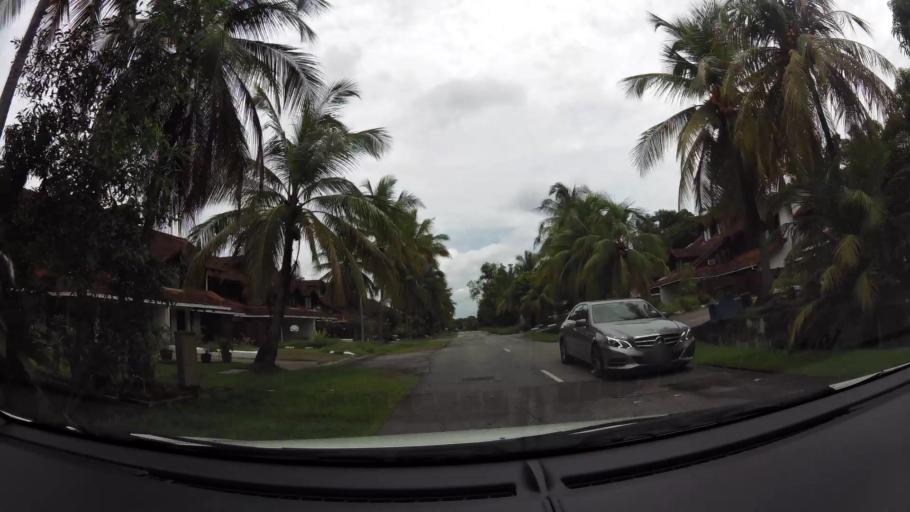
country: BN
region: Brunei and Muara
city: Bandar Seri Begawan
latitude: 4.8937
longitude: 114.9212
